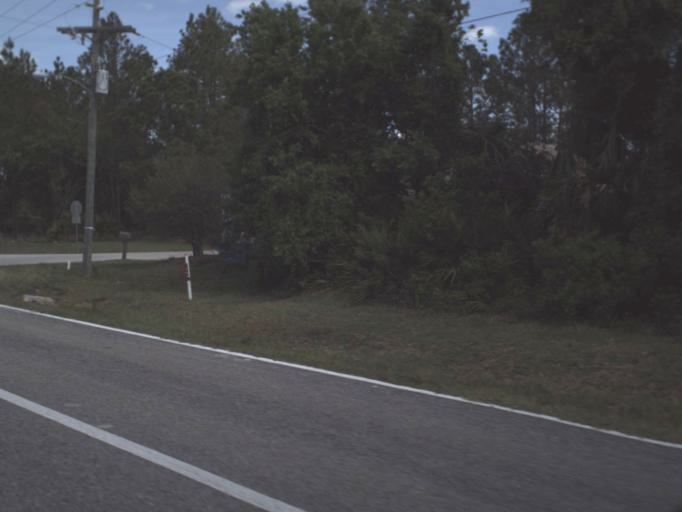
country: US
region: Florida
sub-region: Flagler County
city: Bunnell
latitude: 29.4247
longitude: -81.2188
